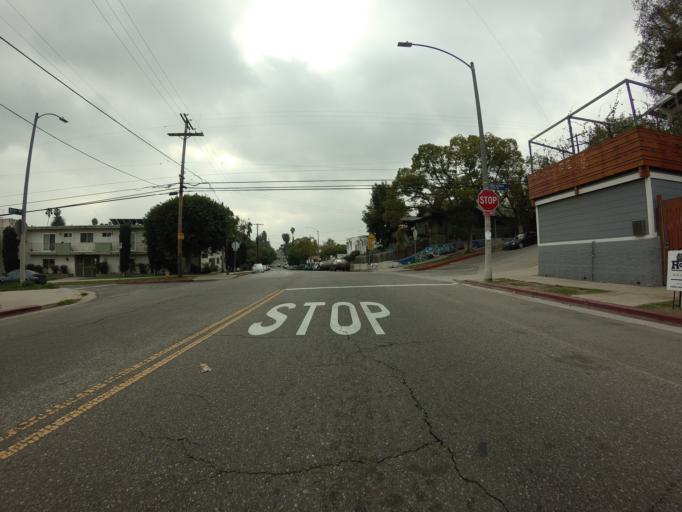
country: US
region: California
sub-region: Los Angeles County
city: Silver Lake
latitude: 34.0792
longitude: -118.2717
